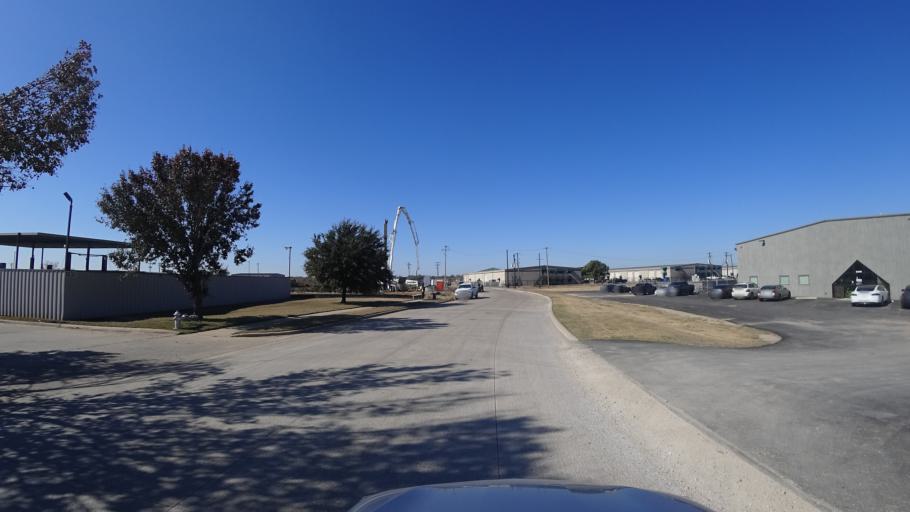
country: US
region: Texas
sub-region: Denton County
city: Lewisville
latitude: 33.0443
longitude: -96.9469
